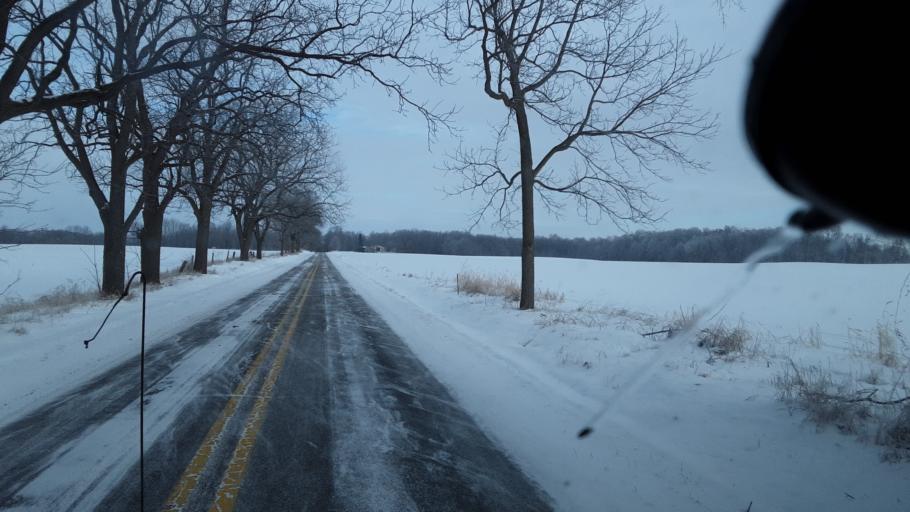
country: US
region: Michigan
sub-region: Ingham County
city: Leslie
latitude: 42.3557
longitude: -84.4826
